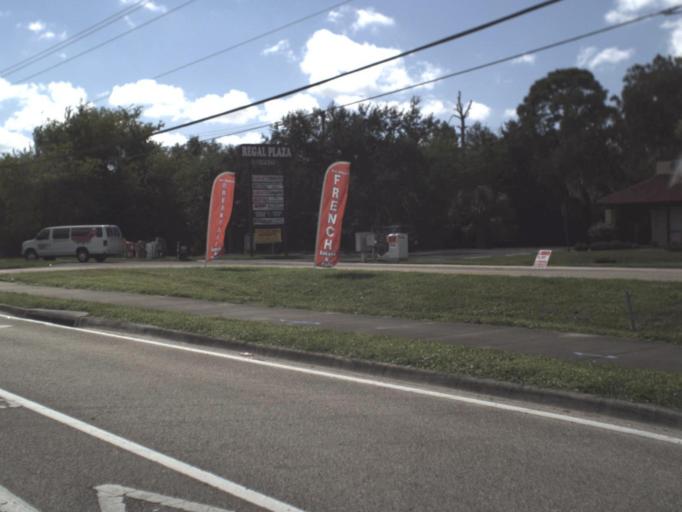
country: US
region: Florida
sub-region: Lee County
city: Villas
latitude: 26.5210
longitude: -81.8691
